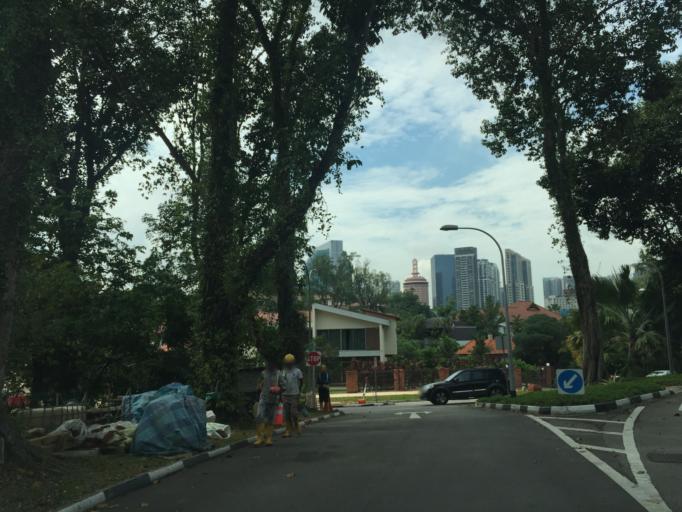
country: SG
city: Singapore
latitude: 1.3223
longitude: 103.8366
